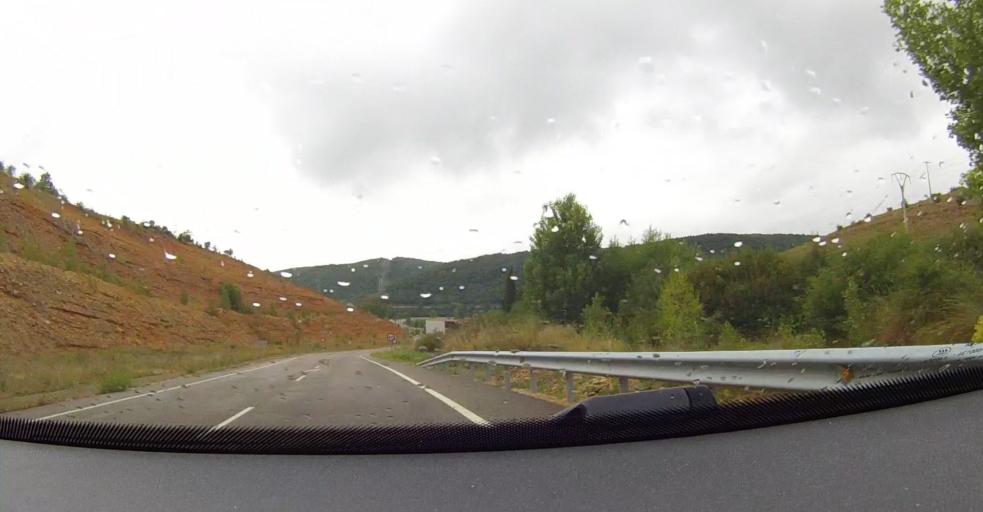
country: ES
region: Castille and Leon
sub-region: Provincia de Leon
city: Cistierna
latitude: 42.7952
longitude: -5.1231
